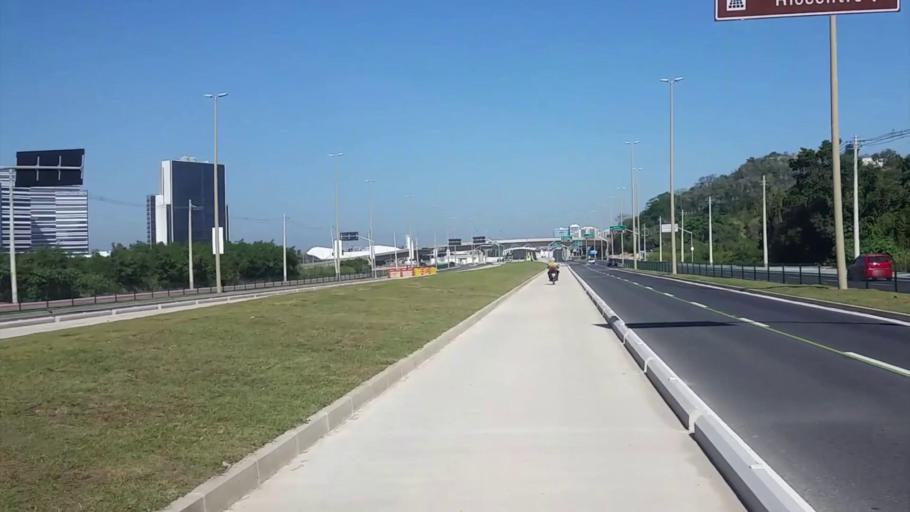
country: BR
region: Rio de Janeiro
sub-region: Nilopolis
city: Nilopolis
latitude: -22.9678
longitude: -43.3981
